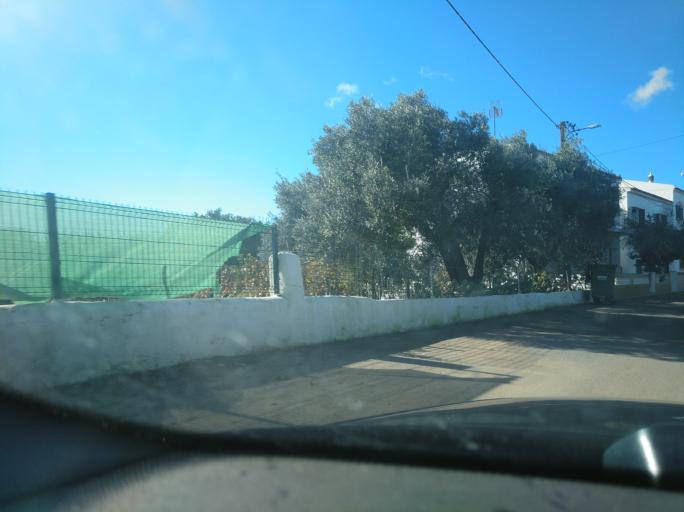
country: PT
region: Faro
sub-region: Tavira
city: Tavira
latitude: 37.1588
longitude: -7.5593
